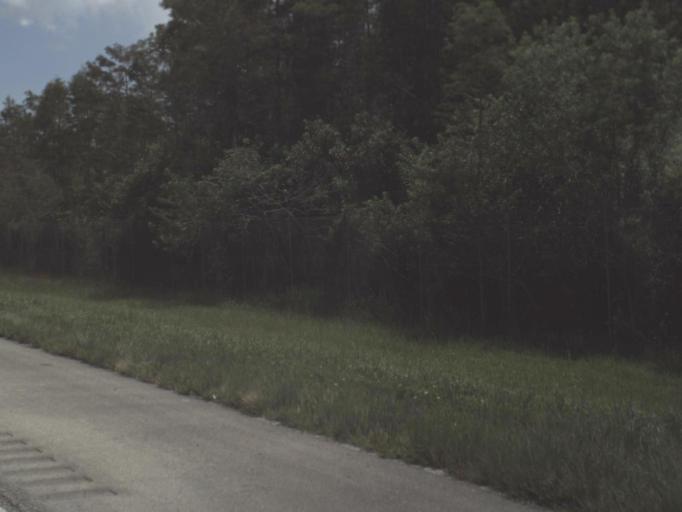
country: US
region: Florida
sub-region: Collier County
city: Immokalee
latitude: 26.1668
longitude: -81.2059
